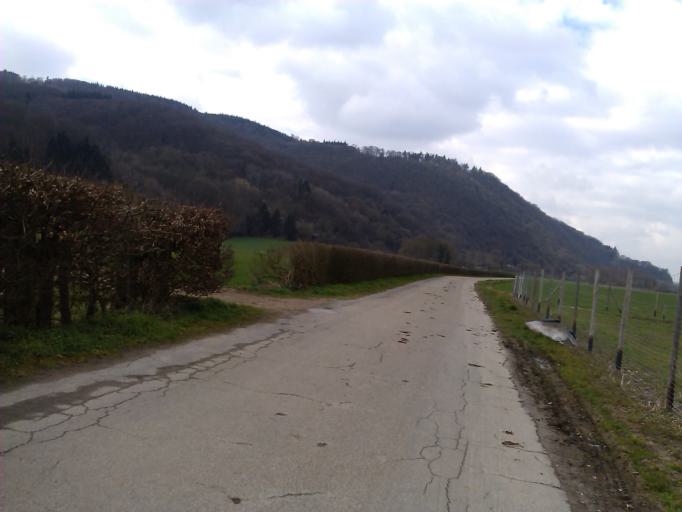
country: DE
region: Rheinland-Pfalz
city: Hammerstein
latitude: 50.4577
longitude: 7.3561
